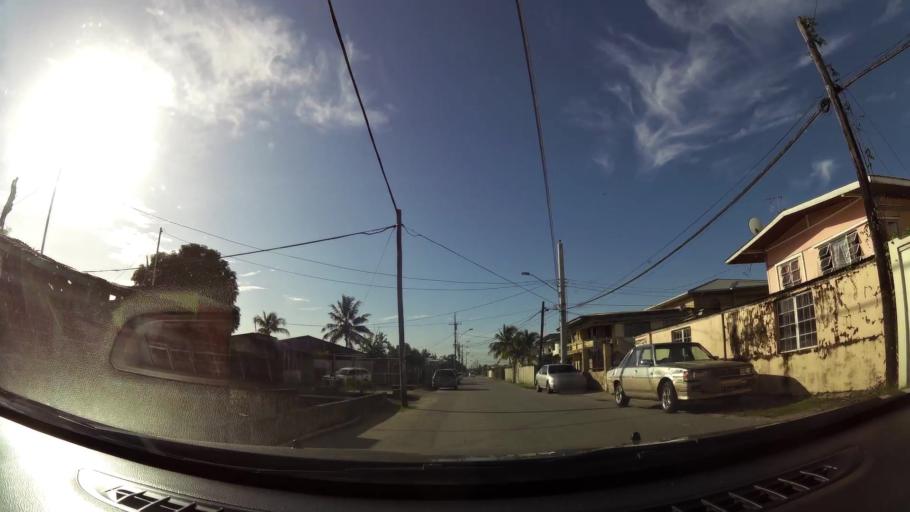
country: TT
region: Tunapuna/Piarco
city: Tunapuna
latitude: 10.5758
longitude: -61.3808
